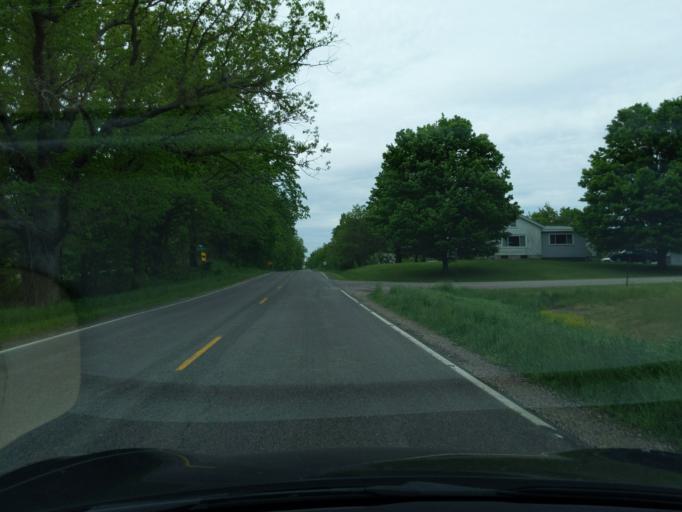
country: US
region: Michigan
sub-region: Ingham County
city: Leslie
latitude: 42.5037
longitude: -84.3562
